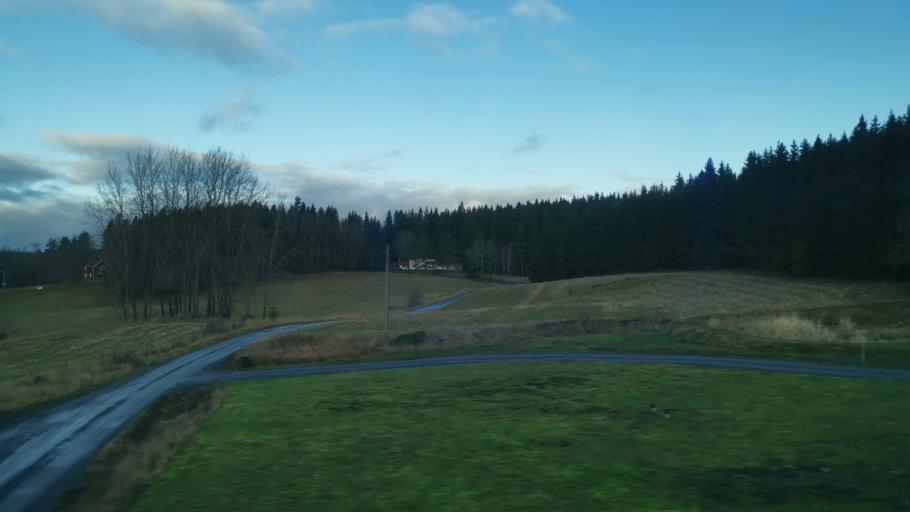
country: SE
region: Soedermanland
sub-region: Flens Kommun
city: Malmkoping
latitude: 59.0600
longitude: 16.6871
